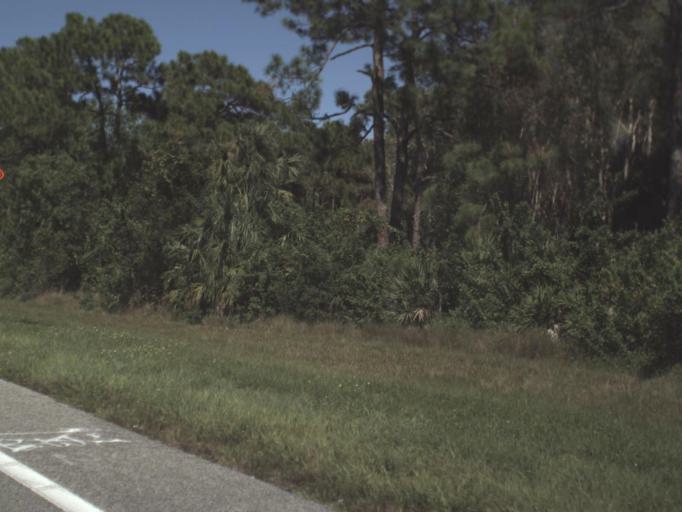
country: US
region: Florida
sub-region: Lee County
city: Palmona Park
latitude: 26.7084
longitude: -81.9009
